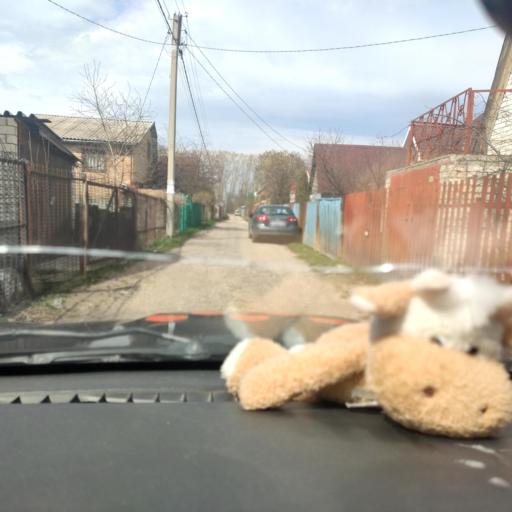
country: RU
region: Samara
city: Tol'yatti
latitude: 53.6037
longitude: 49.2415
